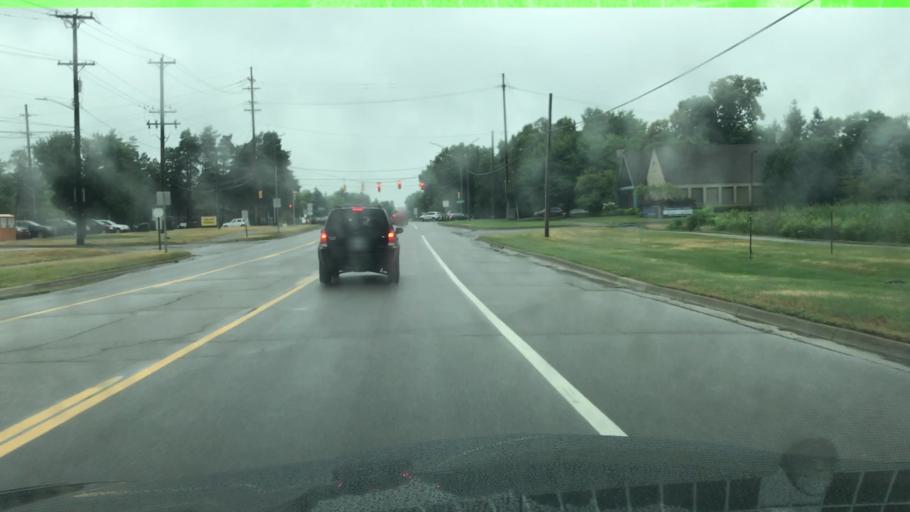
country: US
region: Michigan
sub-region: Oakland County
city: Lake Orion
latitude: 42.7349
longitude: -83.3079
